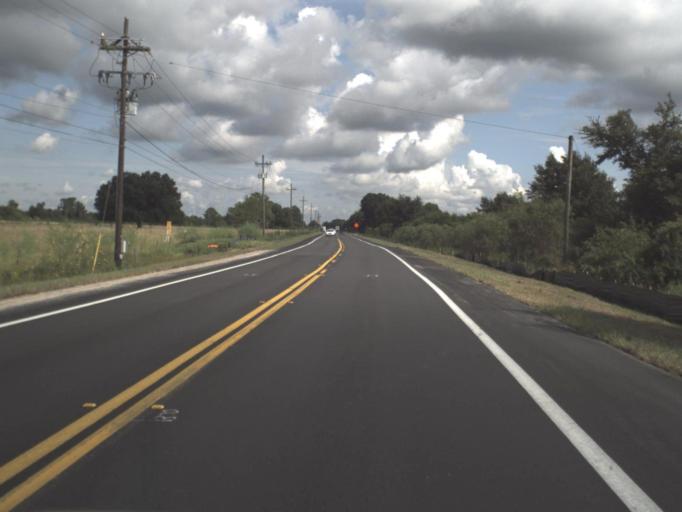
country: US
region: Florida
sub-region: Polk County
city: Combee Settlement
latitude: 28.1077
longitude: -81.9056
